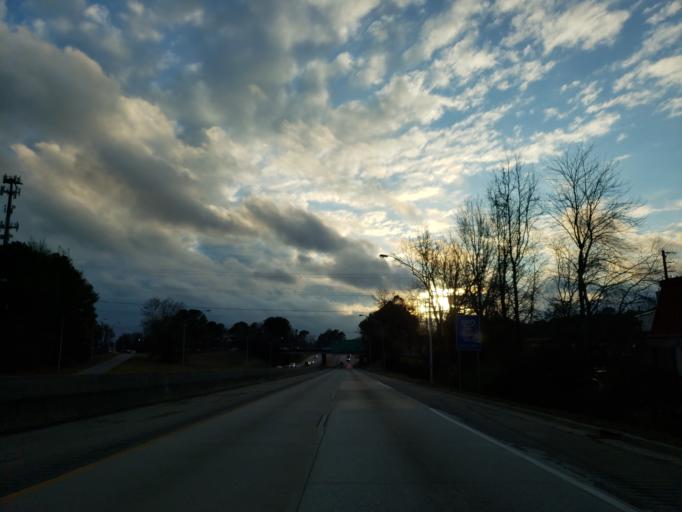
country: US
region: Georgia
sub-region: Fulton County
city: East Point
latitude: 33.6936
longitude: -84.4883
